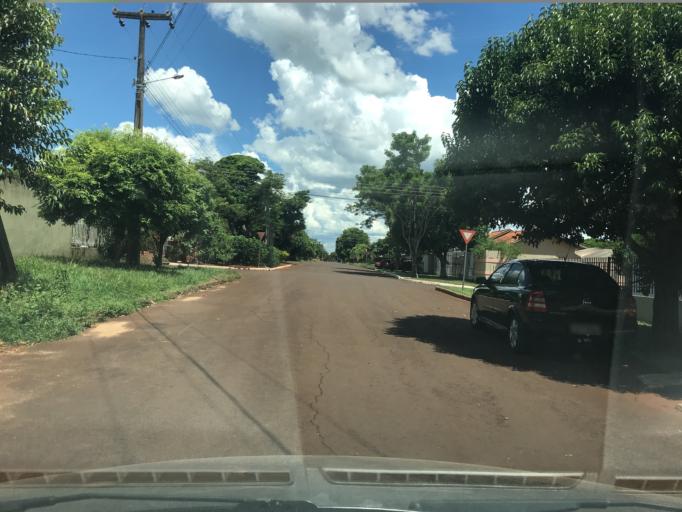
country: BR
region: Parana
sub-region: Palotina
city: Palotina
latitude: -24.2712
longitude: -53.8463
